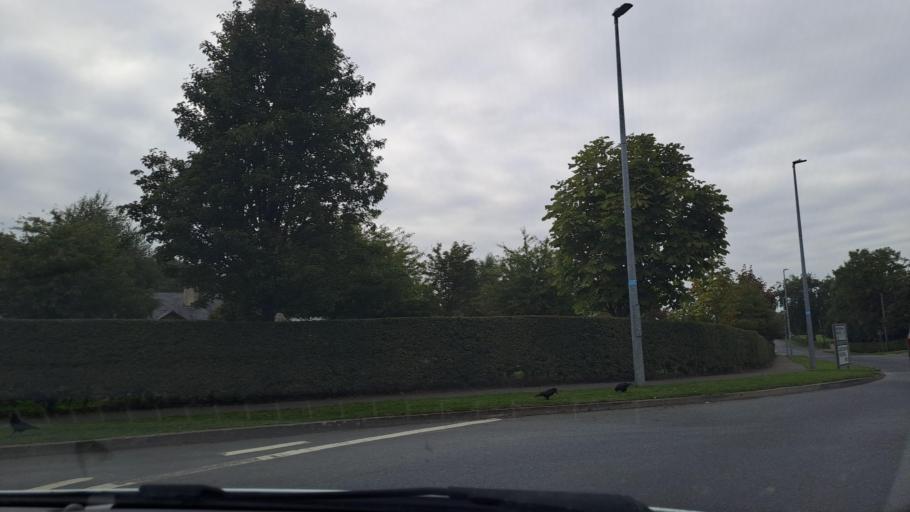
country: IE
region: Ulster
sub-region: County Monaghan
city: Carrickmacross
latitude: 53.9873
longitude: -6.7235
